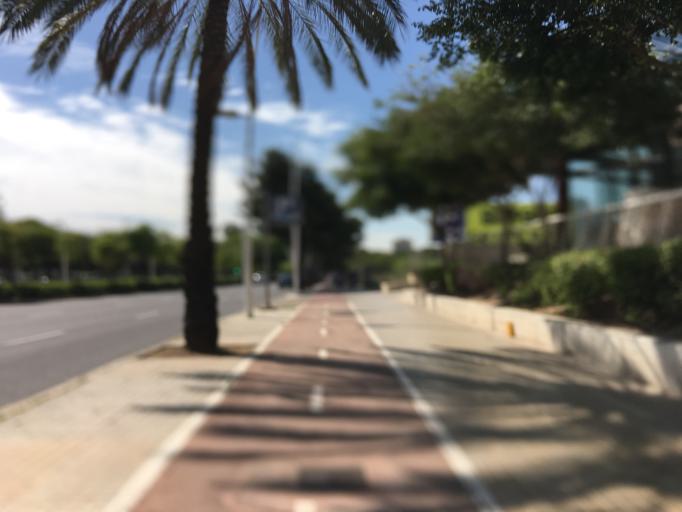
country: ES
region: Valencia
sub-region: Provincia de Valencia
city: Mislata
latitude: 39.4777
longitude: -0.4069
